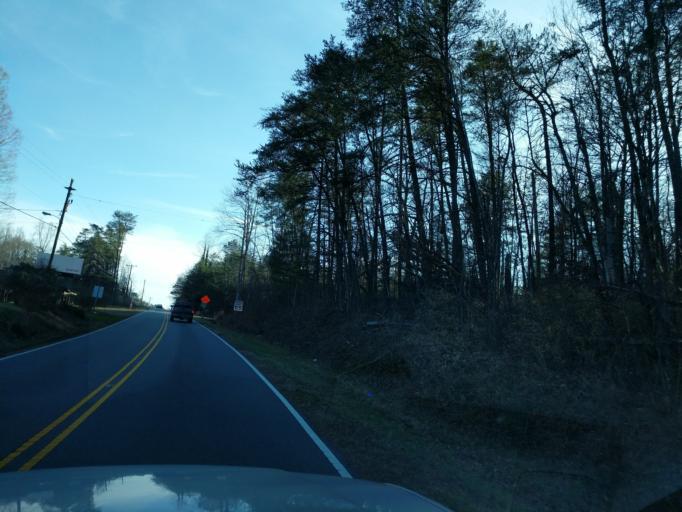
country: US
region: North Carolina
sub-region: Rutherford County
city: Lake Lure
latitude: 35.4029
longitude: -82.1968
